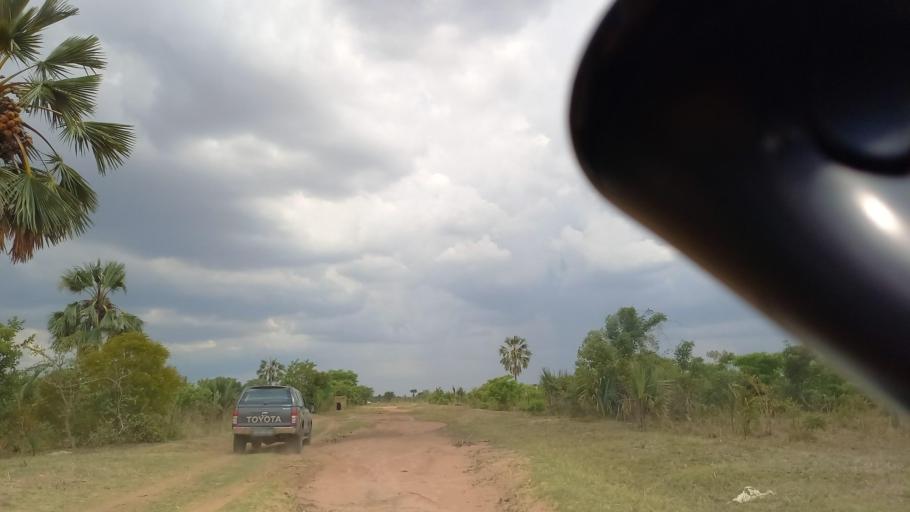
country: ZM
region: Lusaka
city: Kafue
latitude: -15.8338
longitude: 28.0707
